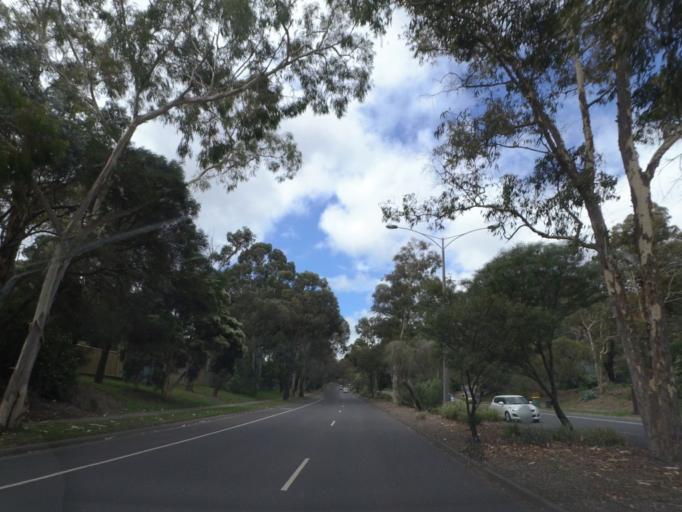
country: AU
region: Victoria
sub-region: Banyule
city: Greensborough
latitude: -37.6959
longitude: 145.1094
